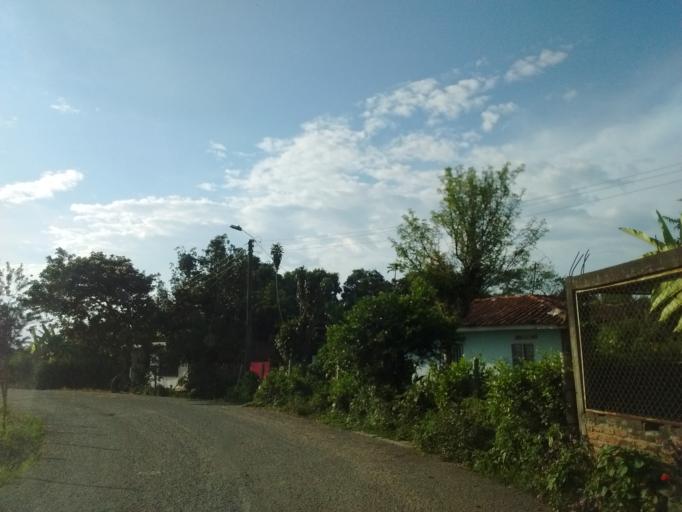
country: CO
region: Cauca
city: Puerto Tejada
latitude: 3.2135
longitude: -76.4443
